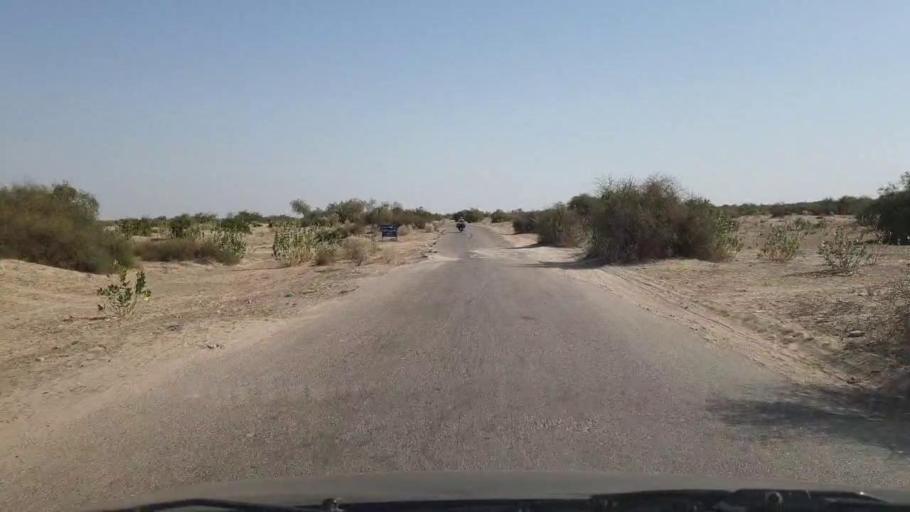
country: PK
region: Sindh
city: Chor
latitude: 25.4963
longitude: 69.8099
